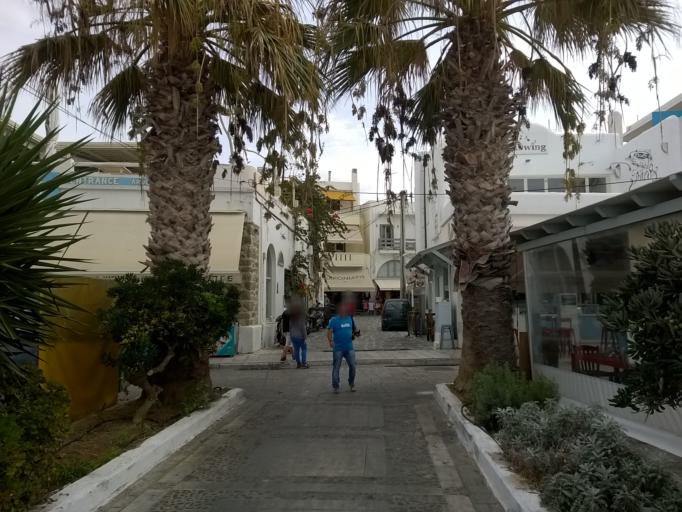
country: GR
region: South Aegean
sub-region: Nomos Kykladon
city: Naxos
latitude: 37.1043
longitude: 25.3752
